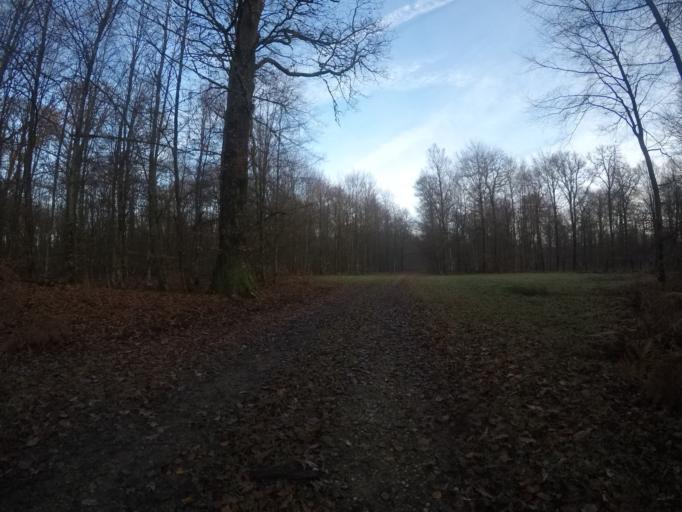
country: BE
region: Wallonia
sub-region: Province du Luxembourg
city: Habay-la-Vieille
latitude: 49.7563
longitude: 5.6690
